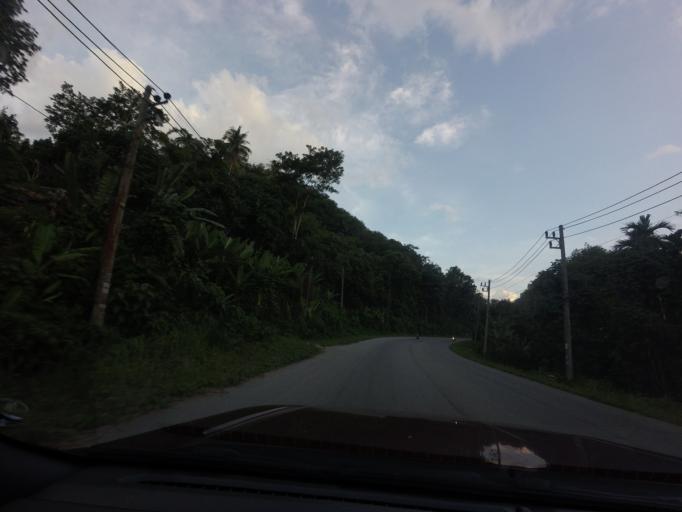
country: TH
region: Yala
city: Than To
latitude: 6.0674
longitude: 101.1982
